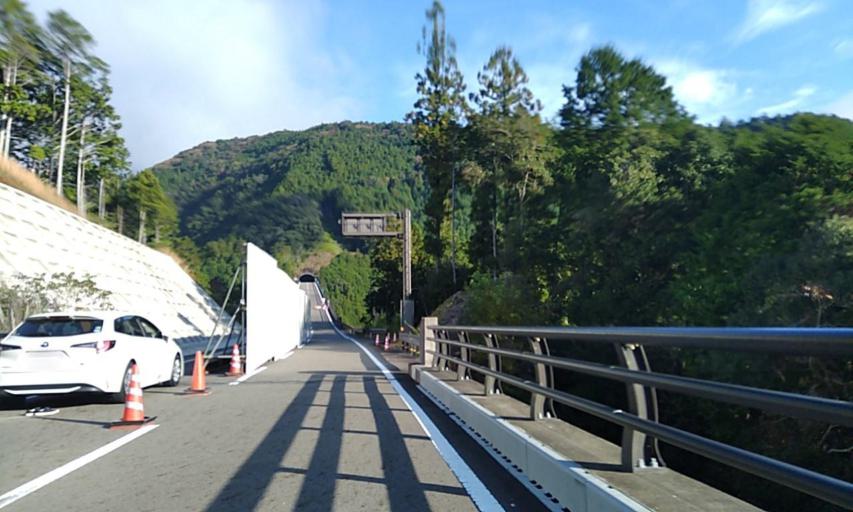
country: JP
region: Wakayama
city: Shingu
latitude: 33.8920
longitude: 135.8798
